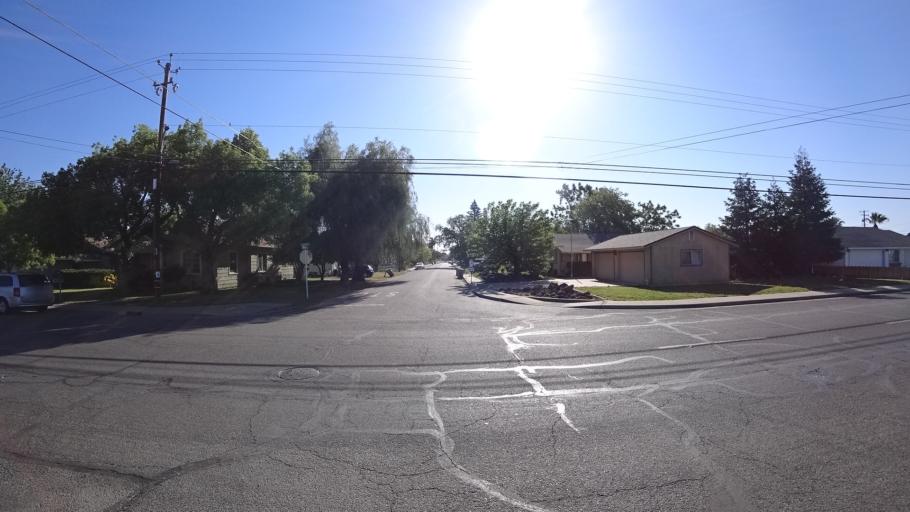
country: US
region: California
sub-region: Glenn County
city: Orland
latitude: 39.7426
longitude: -122.1876
